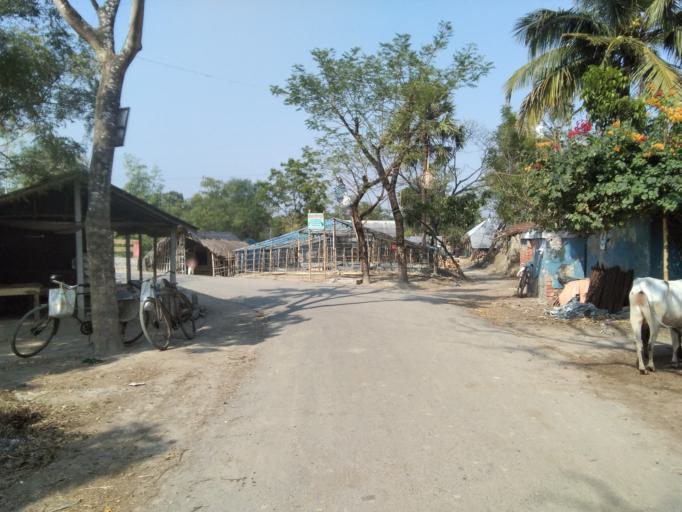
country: IN
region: West Bengal
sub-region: North 24 Parganas
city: Taki
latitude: 22.6379
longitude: 89.0009
